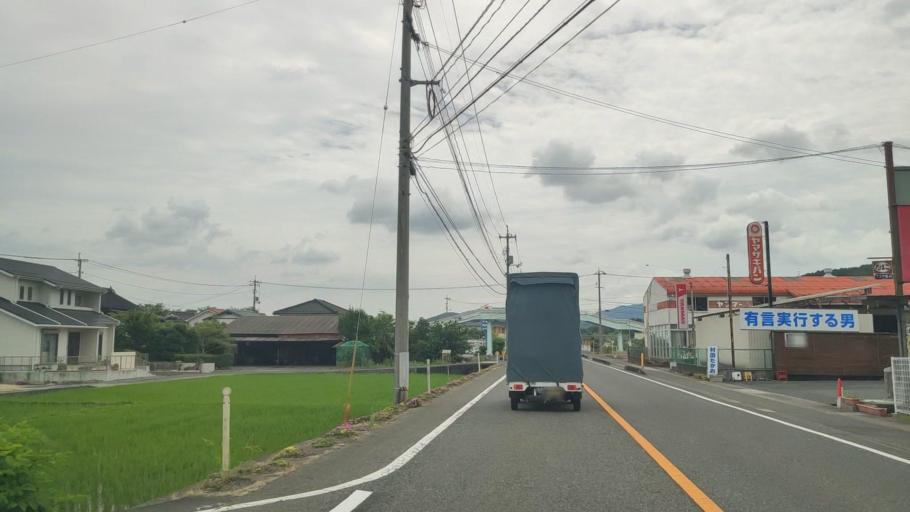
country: JP
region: Okayama
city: Tsuyama
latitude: 35.0545
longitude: 133.9165
